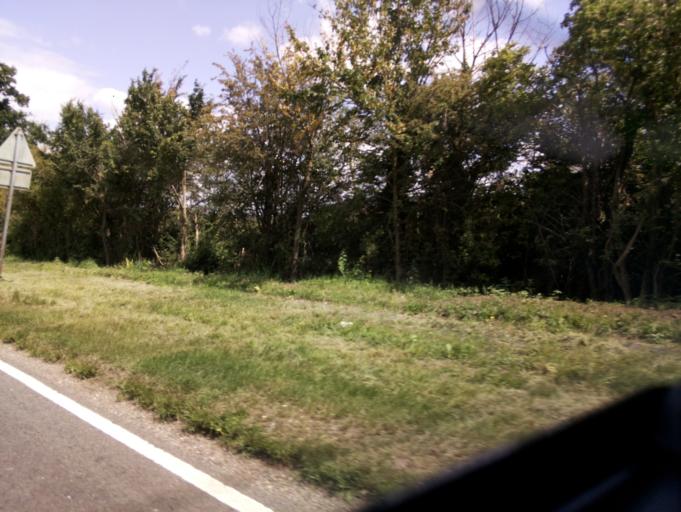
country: GB
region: England
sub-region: Buckinghamshire
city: Aylesbury
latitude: 51.8412
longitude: -0.8195
